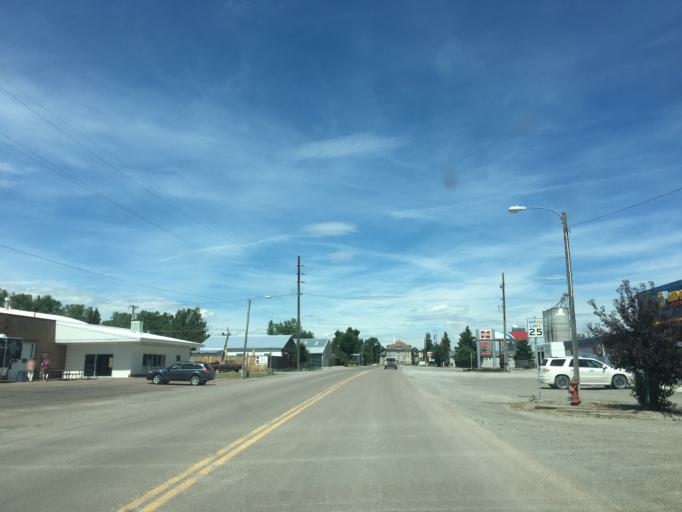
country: US
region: Montana
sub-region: Teton County
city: Choteau
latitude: 47.8075
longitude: -112.1795
